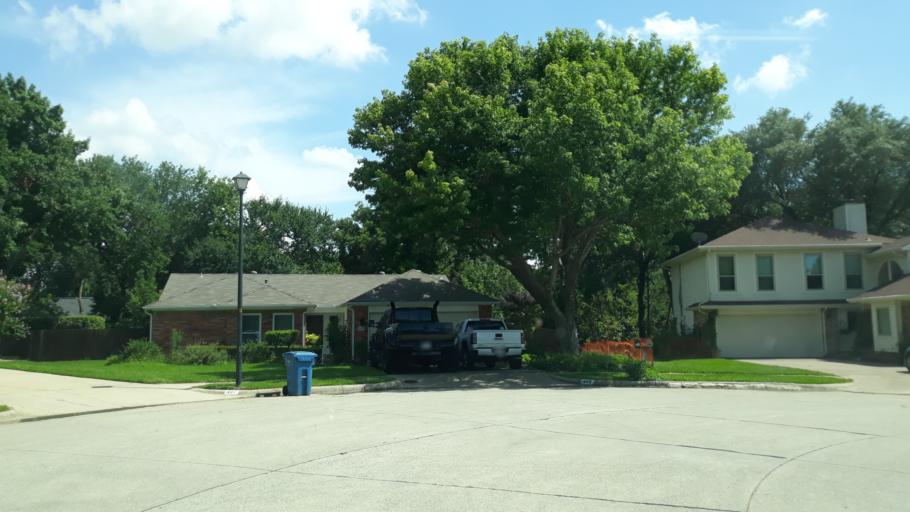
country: US
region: Texas
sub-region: Dallas County
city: Coppell
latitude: 32.9574
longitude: -97.0011
